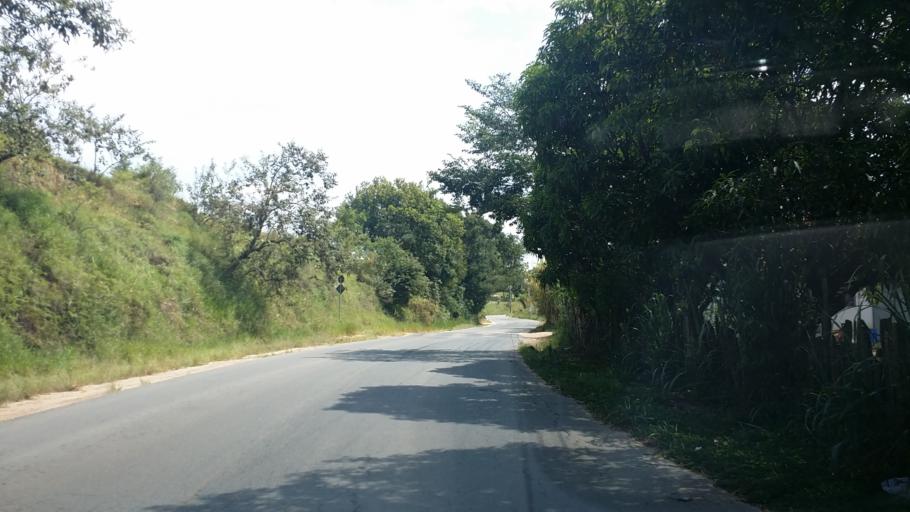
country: BR
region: Sao Paulo
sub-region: Itupeva
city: Itupeva
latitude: -23.1883
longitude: -47.0797
